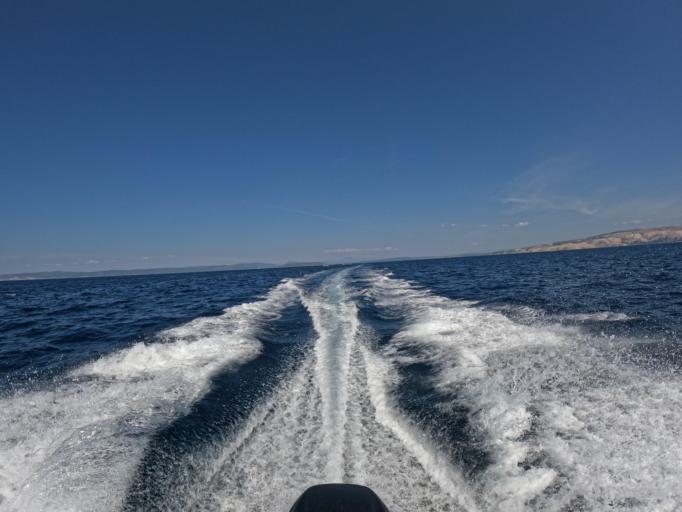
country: HR
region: Primorsko-Goranska
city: Lopar
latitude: 44.8889
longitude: 14.6467
